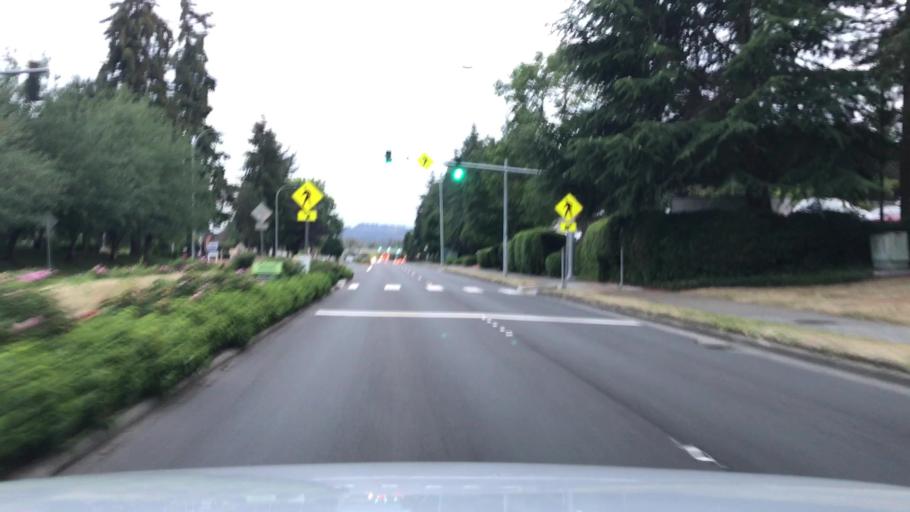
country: US
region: Washington
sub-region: King County
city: Redmond
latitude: 47.6397
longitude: -122.1431
